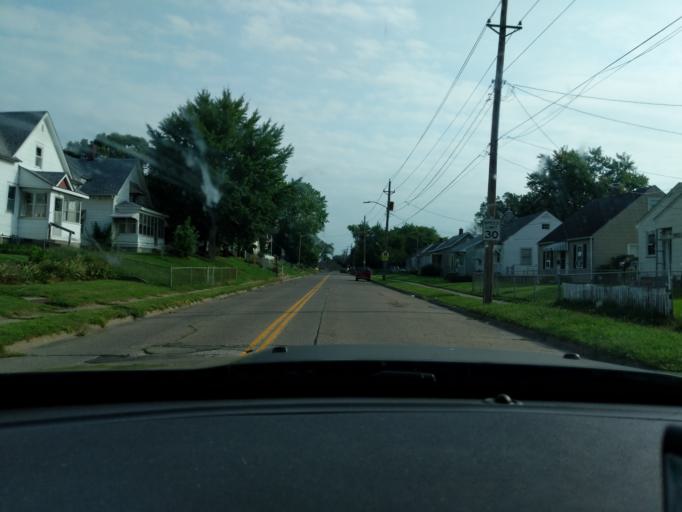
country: US
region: Illinois
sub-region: Rock Island County
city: Rock Island
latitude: 41.5071
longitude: -90.6231
